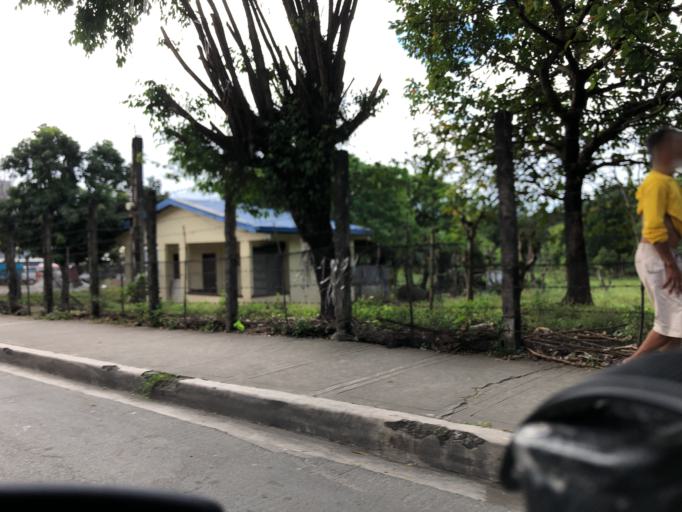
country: PH
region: Central Luzon
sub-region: Province of Bulacan
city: San Jose del Monte
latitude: 14.7407
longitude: 121.0606
